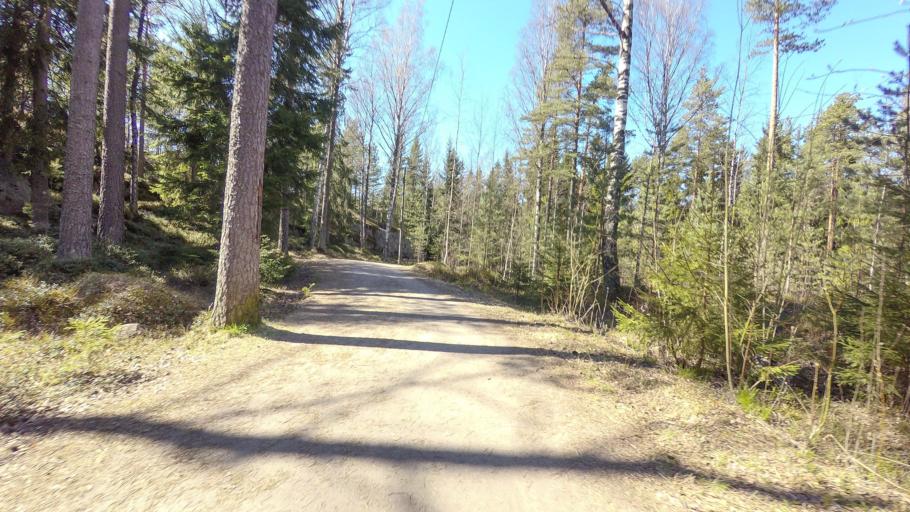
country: FI
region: Uusimaa
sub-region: Helsinki
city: Vantaa
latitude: 60.2260
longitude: 25.1401
